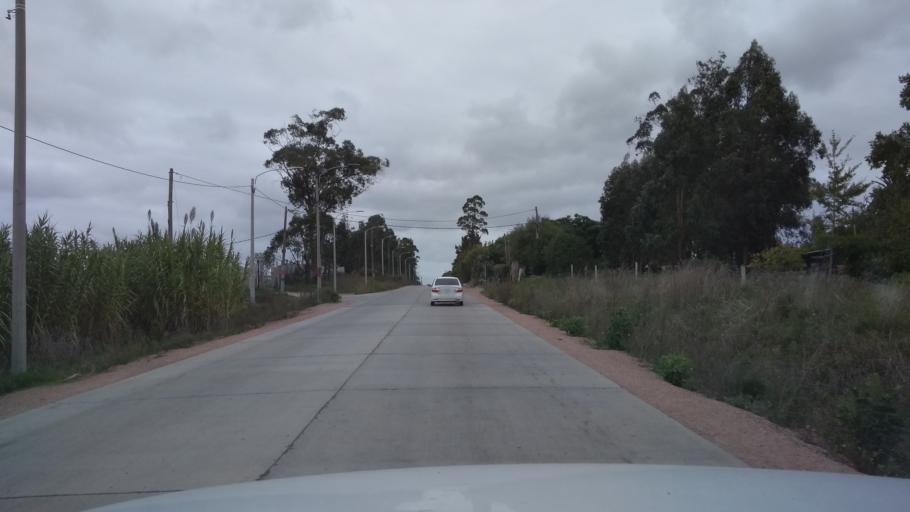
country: UY
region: Canelones
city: Toledo
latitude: -34.7931
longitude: -56.1485
